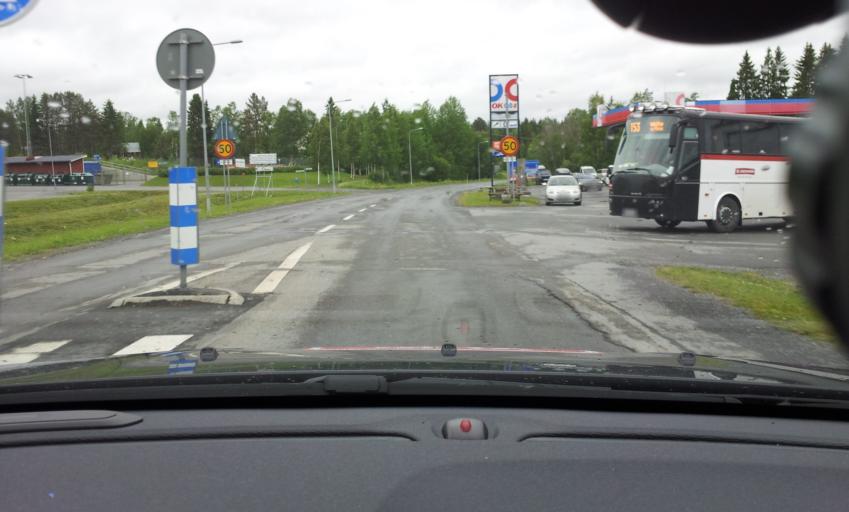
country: SE
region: Jaemtland
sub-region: Krokoms Kommun
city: Krokom
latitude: 63.6713
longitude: 14.6199
